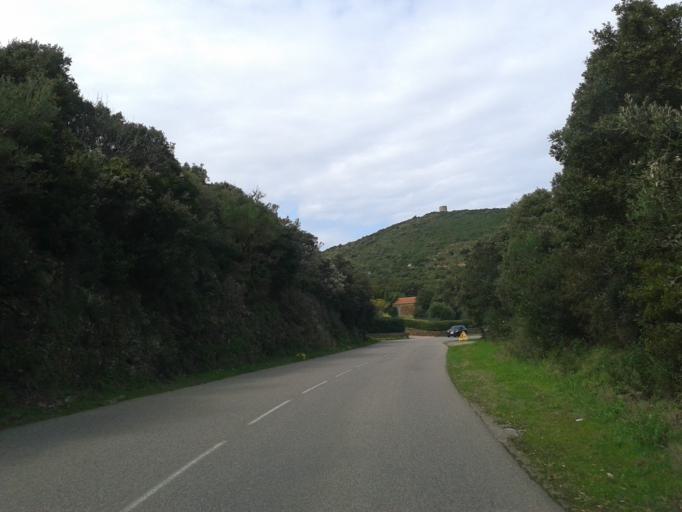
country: FR
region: Corsica
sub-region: Departement de la Haute-Corse
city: Brando
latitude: 42.9492
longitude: 9.4563
